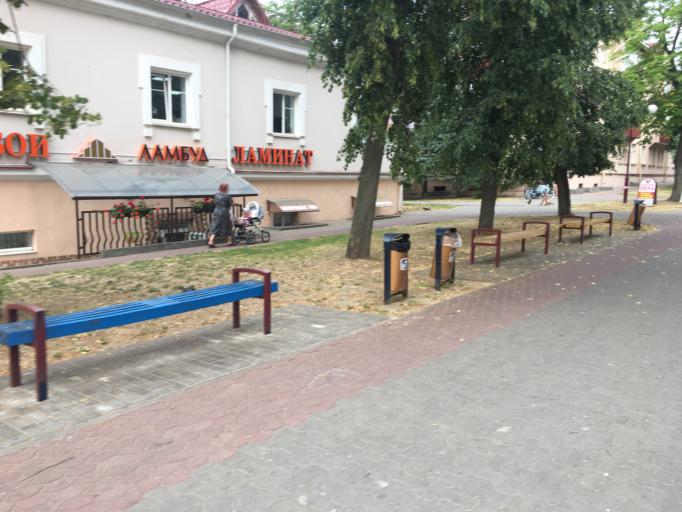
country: BY
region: Grodnenskaya
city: Hrodna
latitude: 53.6760
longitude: 23.8468
